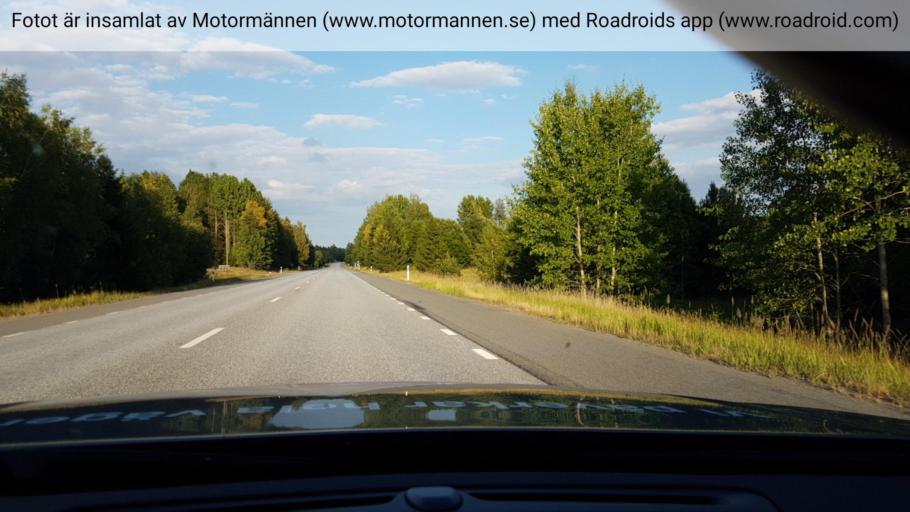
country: SE
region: Uppsala
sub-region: Heby Kommun
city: Morgongava
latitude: 59.8944
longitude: 17.1375
